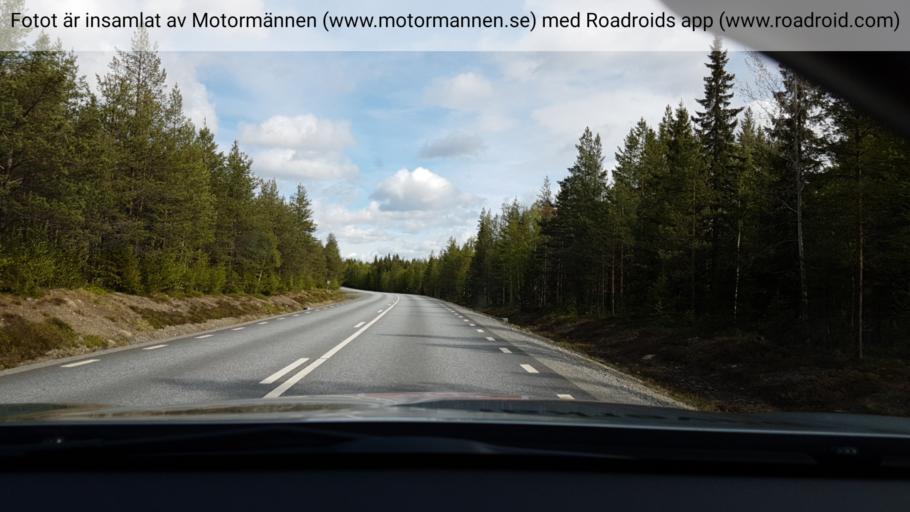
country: SE
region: Vaesterbotten
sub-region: Lycksele Kommun
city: Lycksele
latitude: 64.0742
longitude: 18.3504
